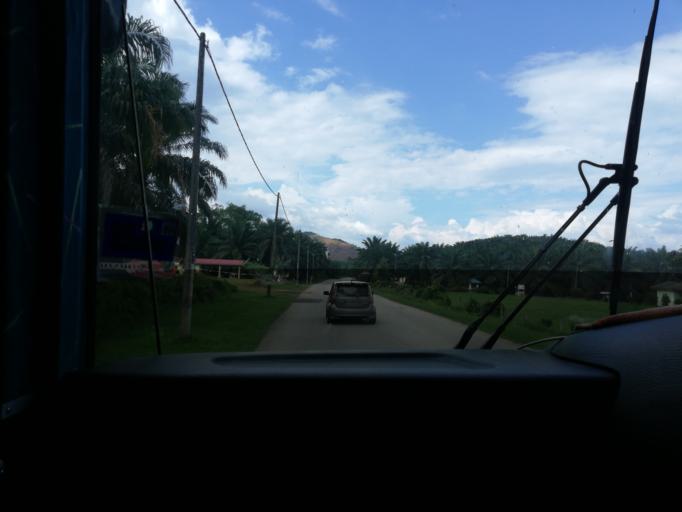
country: MY
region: Kedah
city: Kulim
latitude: 5.2615
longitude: 100.6061
